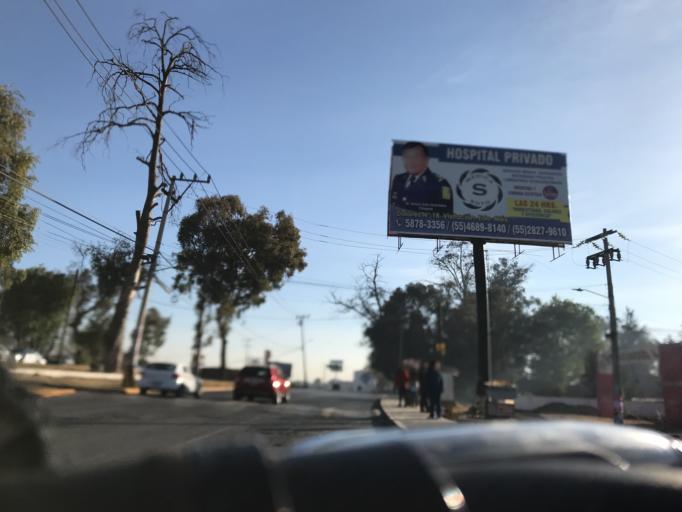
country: MX
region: Mexico
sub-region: Cuautitlan
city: La Trinidad
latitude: 19.6762
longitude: -99.1537
